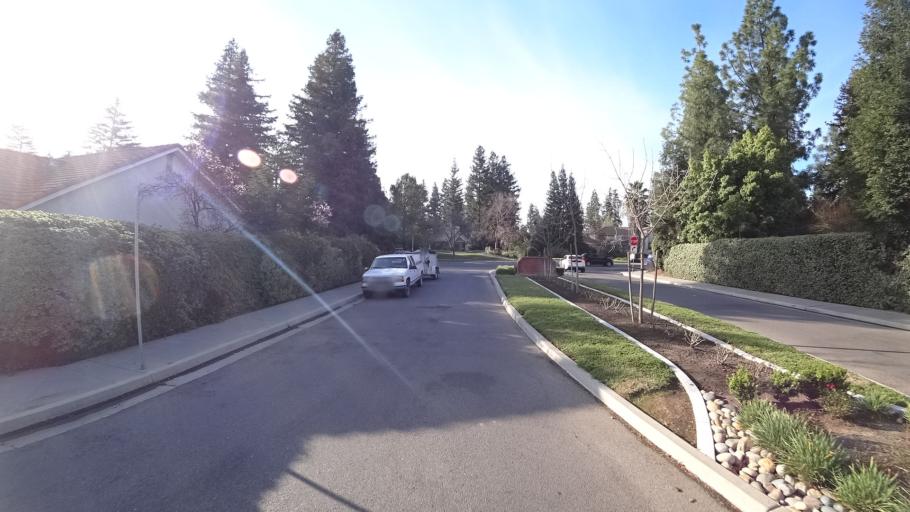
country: US
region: California
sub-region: Fresno County
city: Clovis
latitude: 36.8668
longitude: -119.7775
